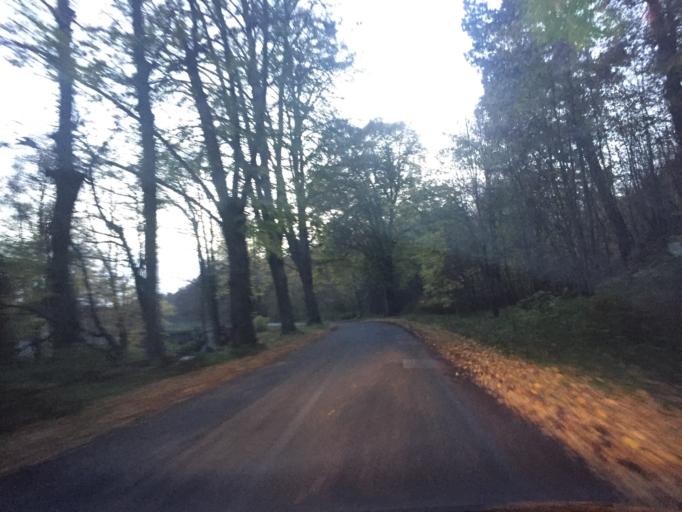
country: DK
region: Capital Region
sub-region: Rudersdal Kommune
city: Trorod
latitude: 55.8078
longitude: 12.5513
